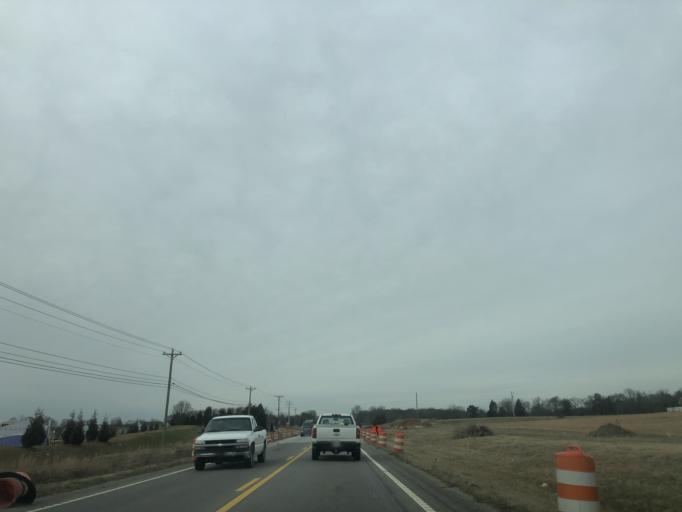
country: US
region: Tennessee
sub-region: Wilson County
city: Mount Juliet
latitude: 36.2502
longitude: -86.4354
